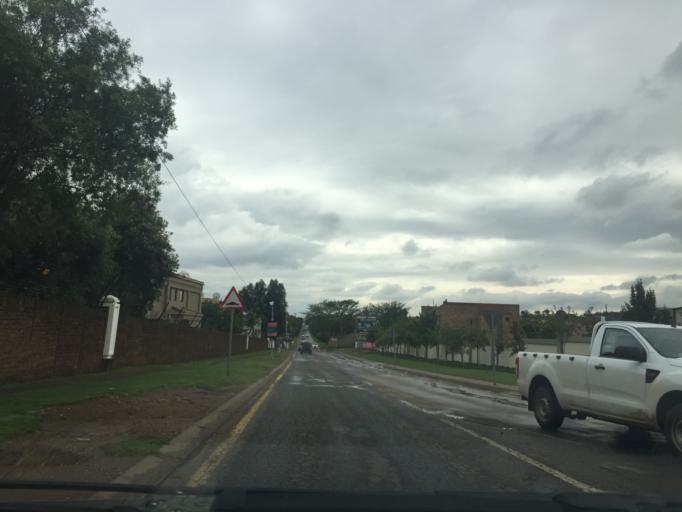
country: ZA
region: Gauteng
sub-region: City of Tshwane Metropolitan Municipality
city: Pretoria
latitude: -25.7811
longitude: 28.3638
